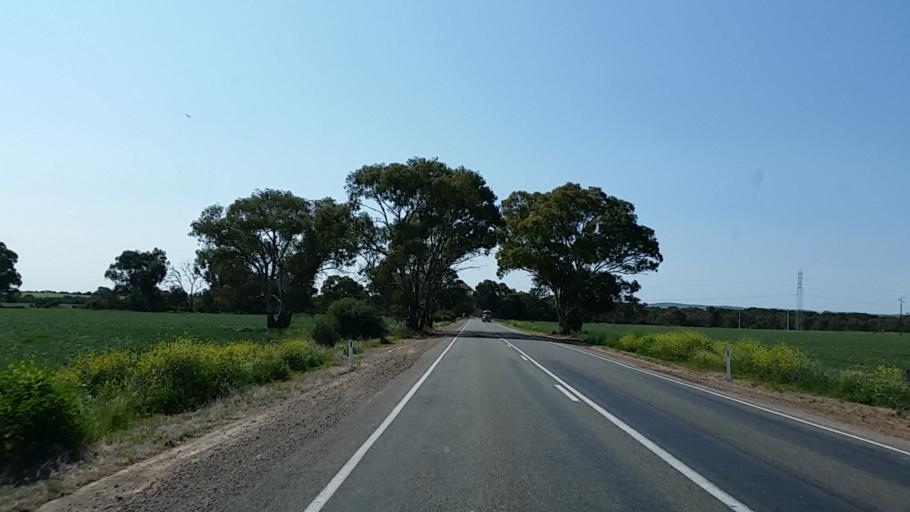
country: AU
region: South Australia
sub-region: Port Pirie City and Dists
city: Crystal Brook
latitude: -33.2642
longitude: 138.3362
